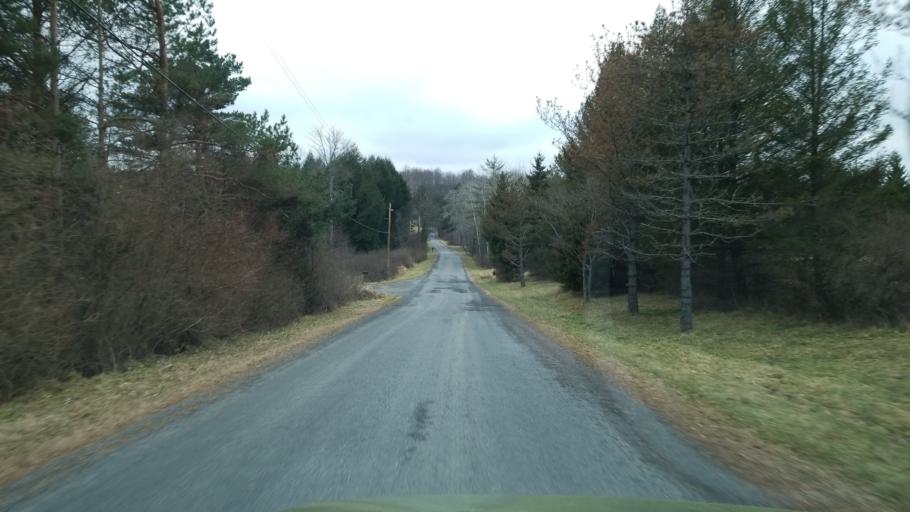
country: US
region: Pennsylvania
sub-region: Jefferson County
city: Falls Creek
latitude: 41.1799
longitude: -78.8095
